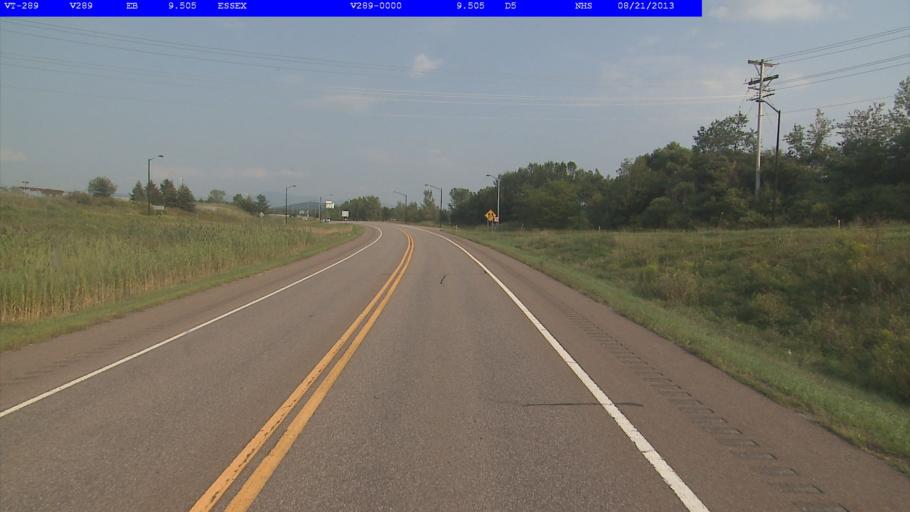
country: US
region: Vermont
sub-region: Chittenden County
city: Essex Junction
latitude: 44.5066
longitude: -73.0877
